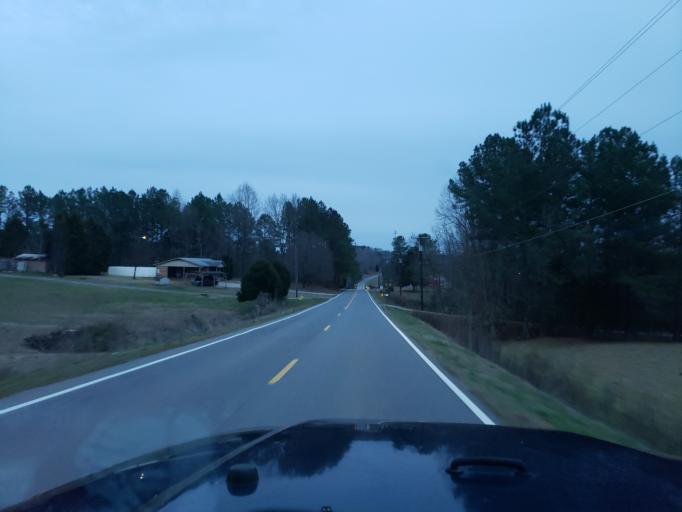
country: US
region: North Carolina
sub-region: Cleveland County
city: White Plains
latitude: 35.2266
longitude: -81.4596
